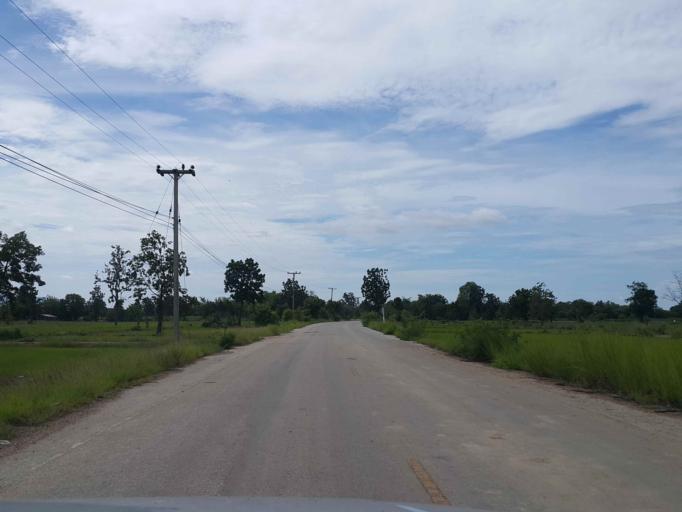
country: TH
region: Sukhothai
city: Ban Dan Lan Hoi
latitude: 17.0928
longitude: 99.4764
